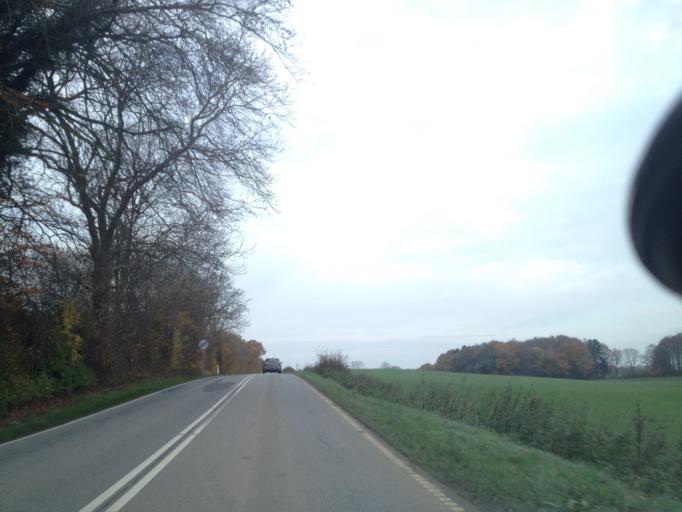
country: DK
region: South Denmark
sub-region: Assens Kommune
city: Vissenbjerg
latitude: 55.4495
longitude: 10.1232
